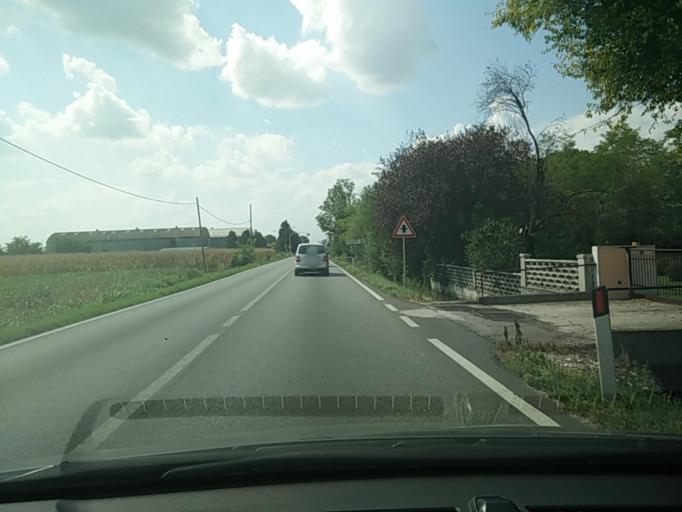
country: IT
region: Veneto
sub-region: Provincia di Treviso
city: Ponzano
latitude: 45.7302
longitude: 12.2211
